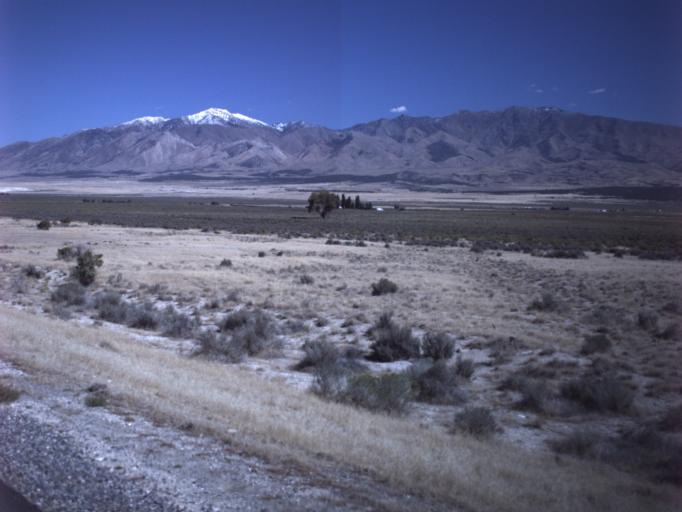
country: US
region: Utah
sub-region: Tooele County
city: Grantsville
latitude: 40.2877
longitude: -112.7421
